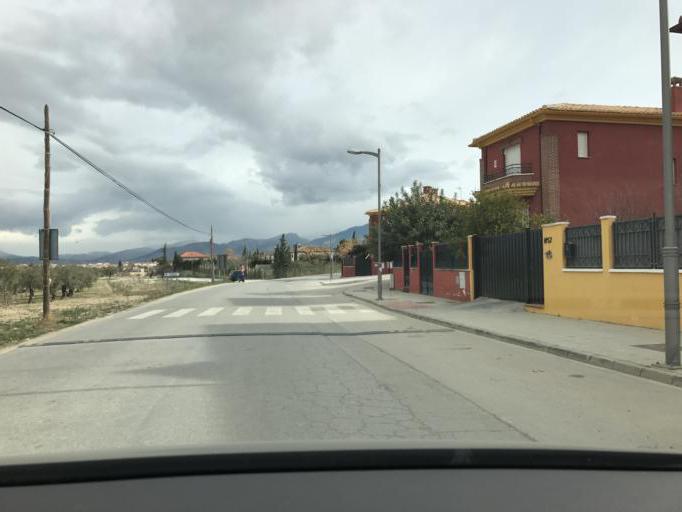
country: ES
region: Andalusia
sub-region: Provincia de Granada
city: Alhendin
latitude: 37.1064
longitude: -3.6590
